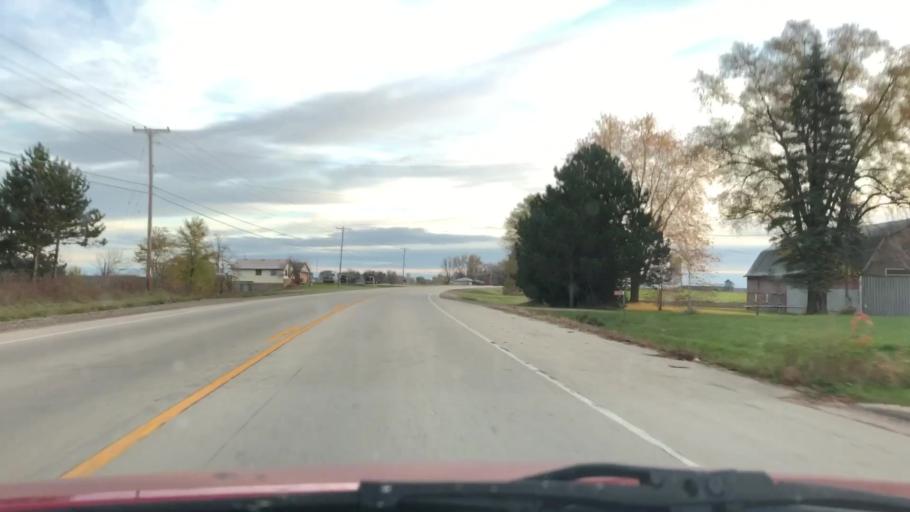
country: US
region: Wisconsin
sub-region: Brown County
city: Oneida
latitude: 44.4188
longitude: -88.2525
